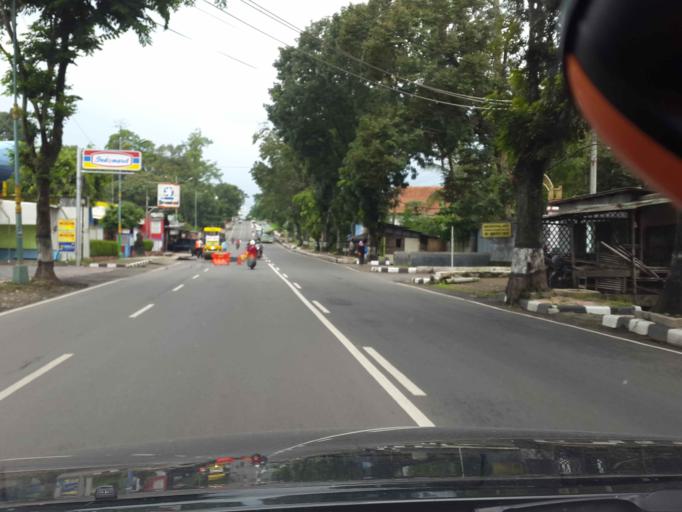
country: ID
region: Central Java
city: Salatiga
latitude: -7.3559
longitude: 110.5129
